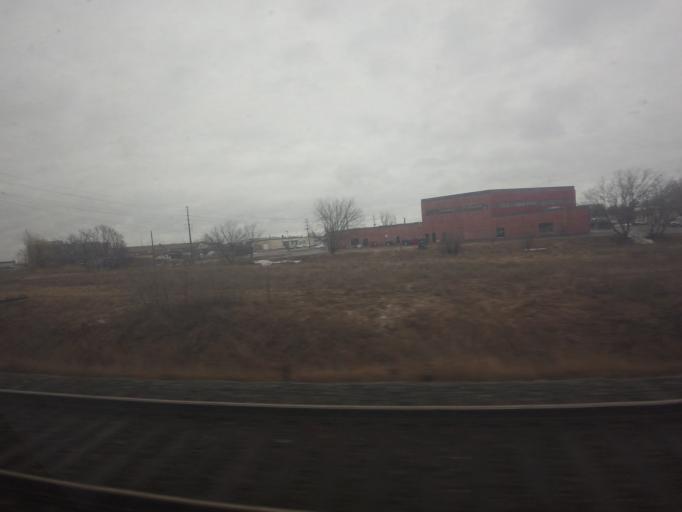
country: CA
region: Ontario
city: Kingston
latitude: 44.2397
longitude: -76.5722
